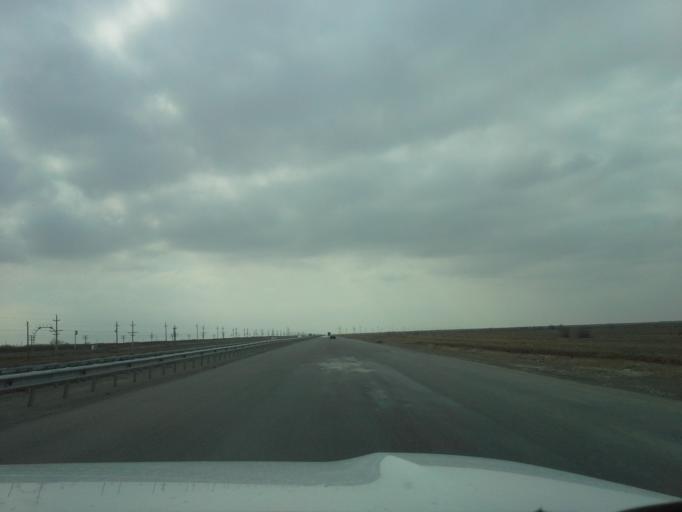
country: IR
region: Razavi Khorasan
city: Kalat-e Naderi
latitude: 37.2209
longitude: 60.1169
